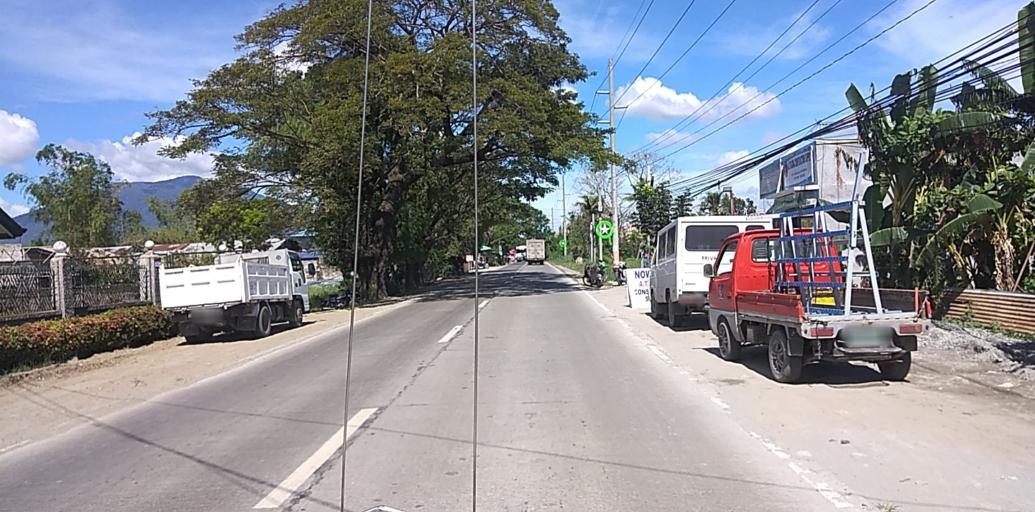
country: PH
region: Central Luzon
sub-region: Province of Pampanga
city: Santa Ana
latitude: 15.1221
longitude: 120.7758
